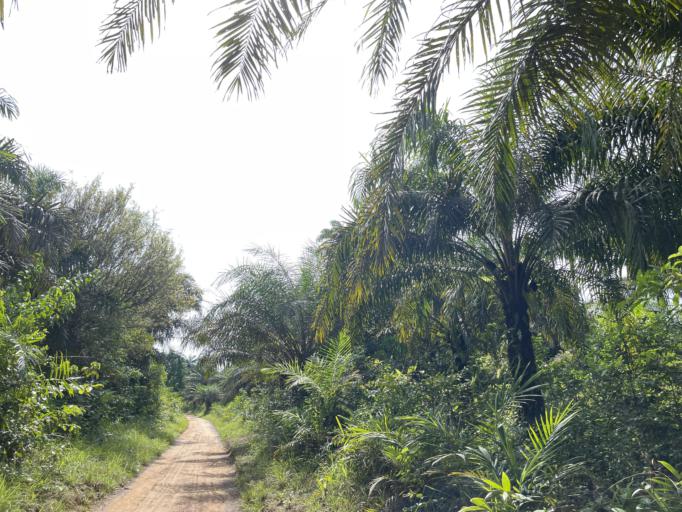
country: SL
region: Southern Province
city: Pujehun
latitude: 7.4084
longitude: -11.7739
